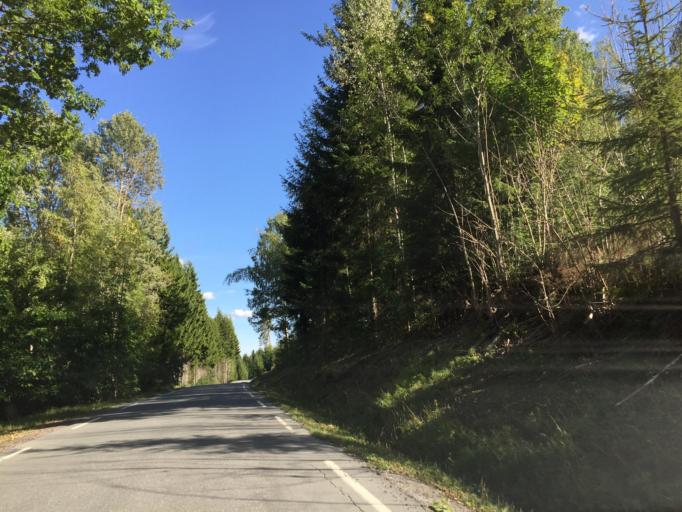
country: NO
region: Buskerud
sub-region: Ovre Eiker
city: Hokksund
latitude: 59.6601
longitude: 9.9016
